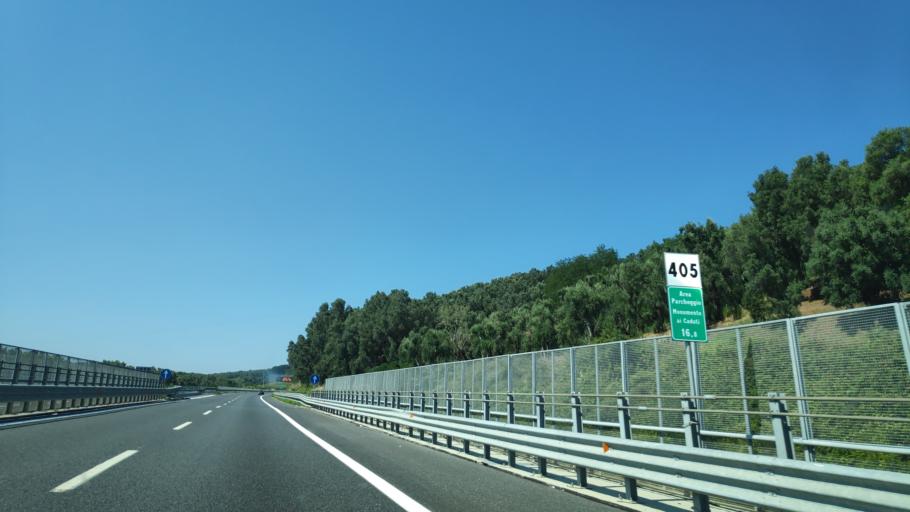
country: IT
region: Calabria
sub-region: Provincia di Reggio Calabria
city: Seminara
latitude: 38.3371
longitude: 15.8627
